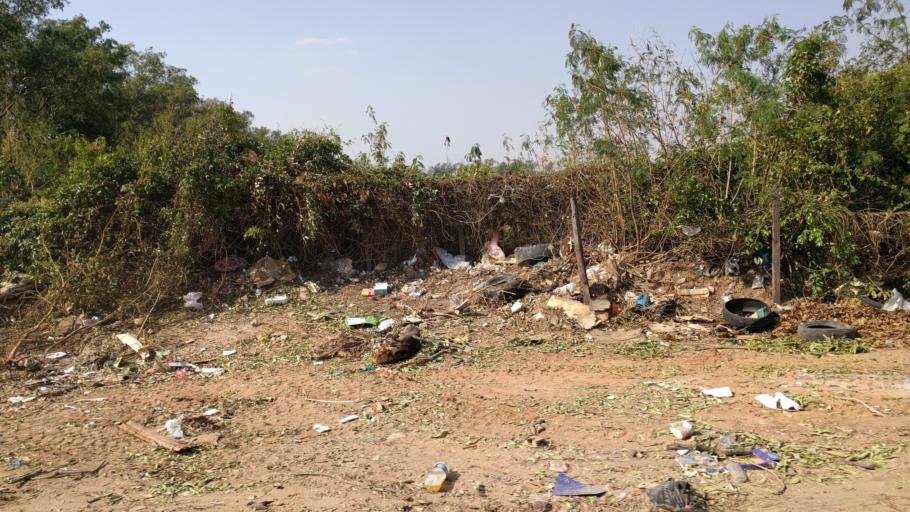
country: BO
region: Santa Cruz
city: Santa Cruz de la Sierra
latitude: -17.8209
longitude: -63.1629
